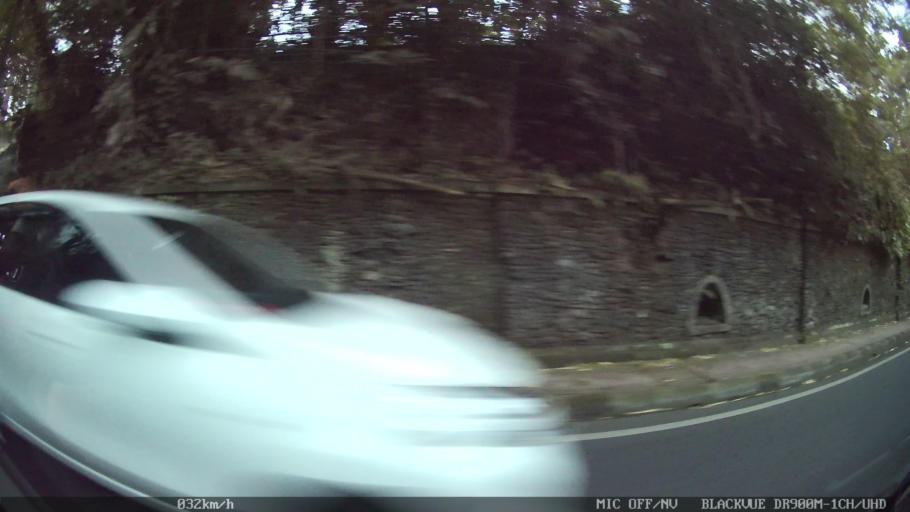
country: ID
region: Bali
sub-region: Kabupaten Gianyar
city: Ubud
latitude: -8.5012
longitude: 115.2528
